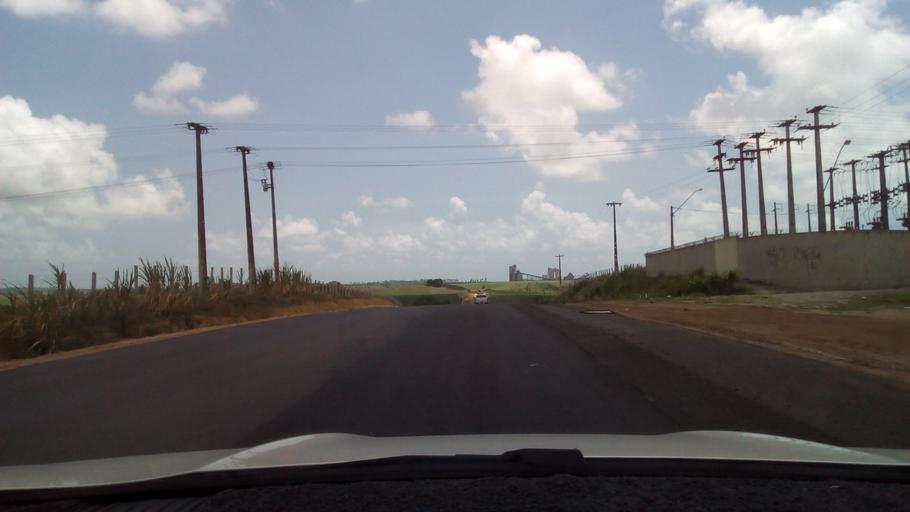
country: BR
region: Paraiba
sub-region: Caapora
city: Caapora
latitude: -7.5138
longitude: -34.8884
